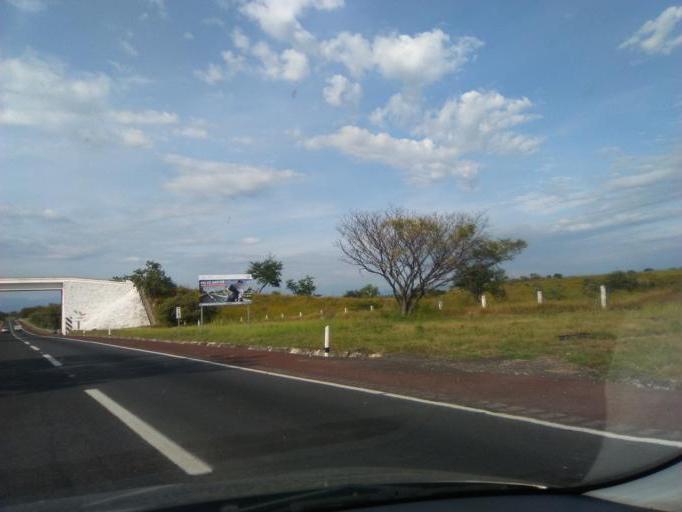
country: MX
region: Morelos
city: Ahuehuetzingo
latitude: 18.6592
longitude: -99.2951
